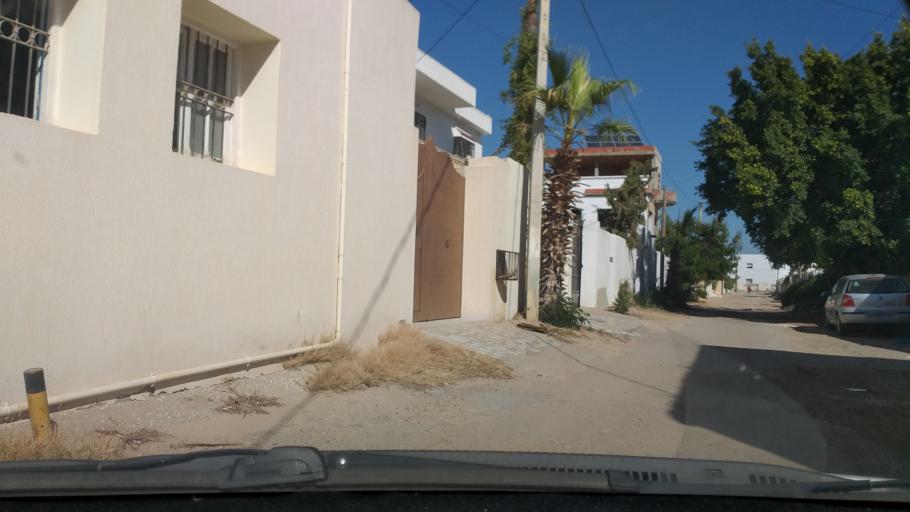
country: TN
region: Safaqis
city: Al Qarmadah
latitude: 34.7694
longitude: 10.7723
